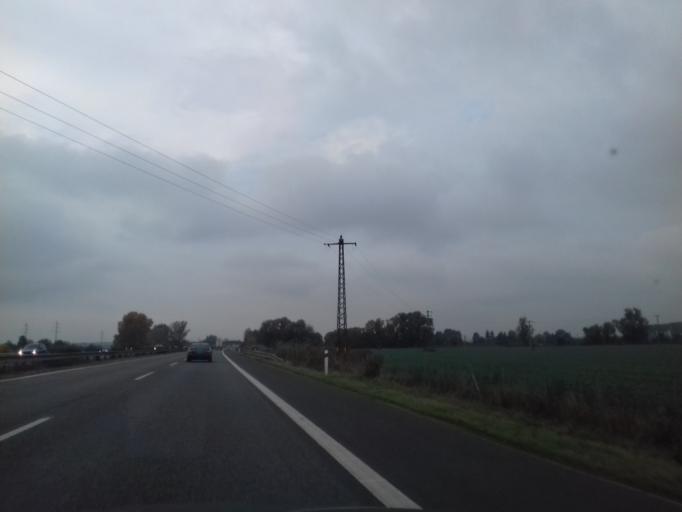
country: SK
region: Bratislavsky
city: Stupava
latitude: 48.2301
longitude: 17.0225
